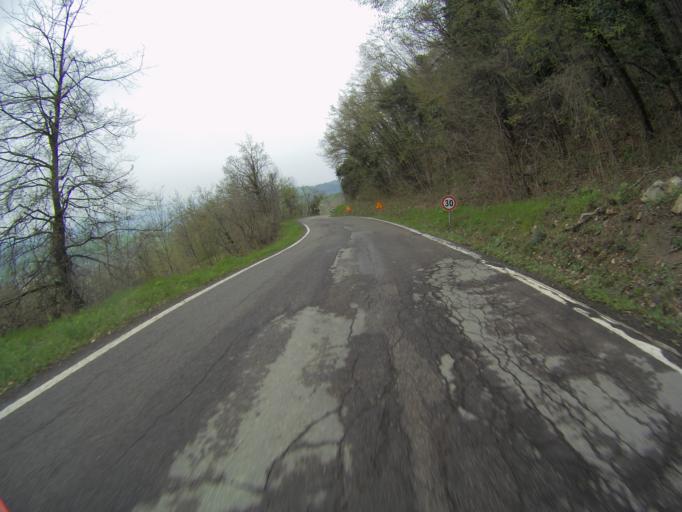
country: IT
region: Emilia-Romagna
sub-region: Provincia di Reggio Emilia
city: Ciano d'Enza
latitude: 44.5649
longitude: 10.4483
